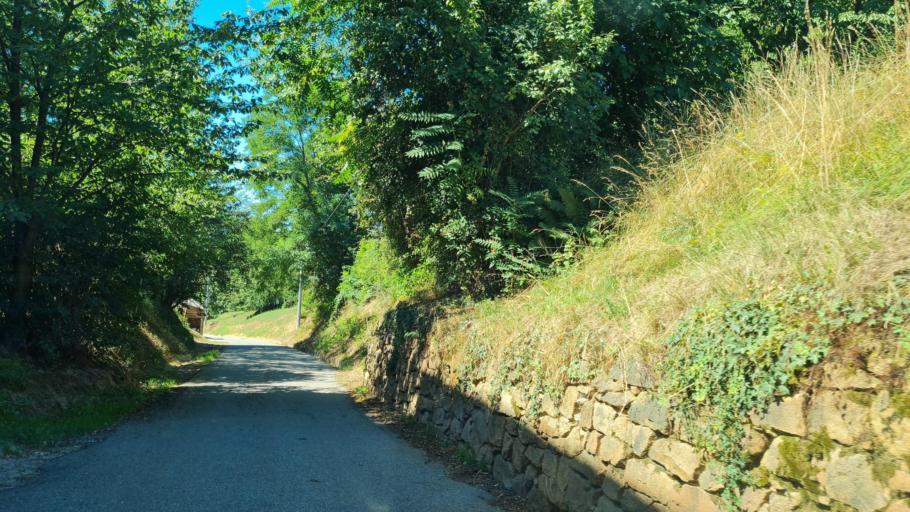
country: IT
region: Piedmont
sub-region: Provincia di Biella
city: Masserano
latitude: 45.5866
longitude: 8.2201
